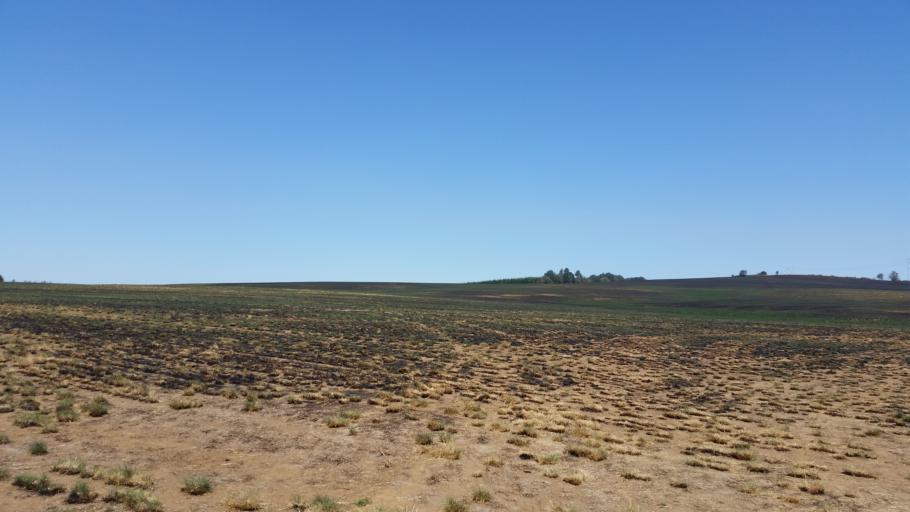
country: US
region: Oregon
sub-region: Marion County
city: Sublimity
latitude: 44.8658
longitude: -122.8251
